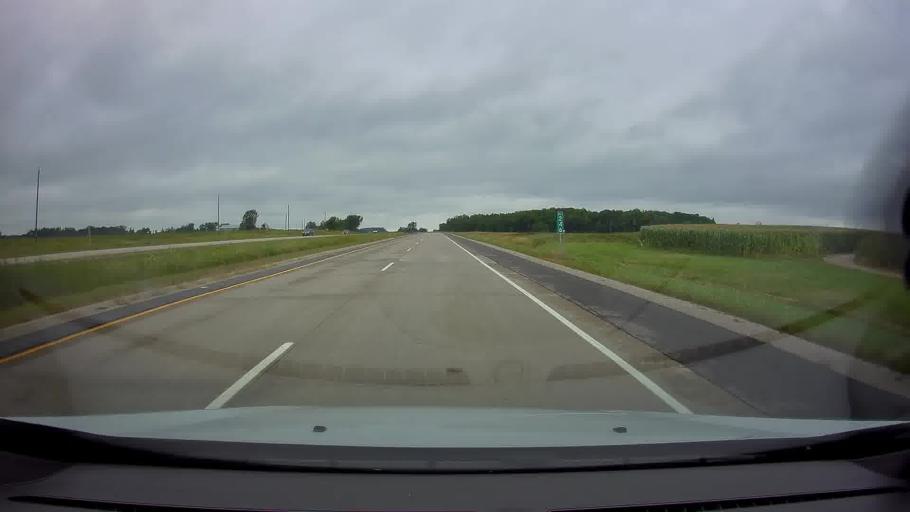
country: US
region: Wisconsin
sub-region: Brown County
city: Pulaski
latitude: 44.6251
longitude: -88.2731
